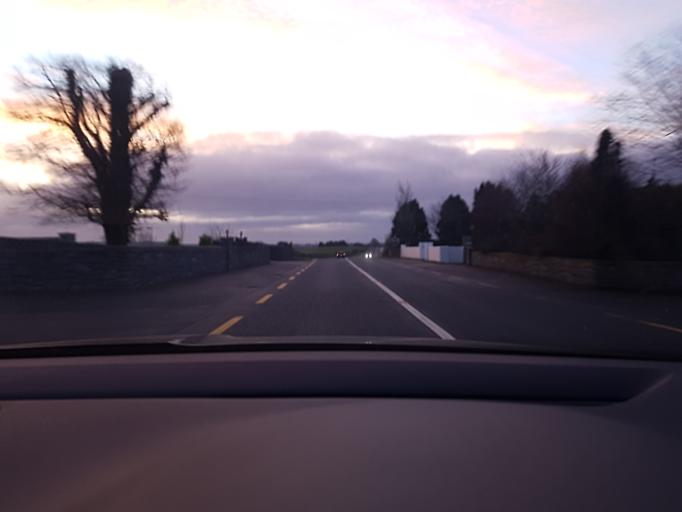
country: IE
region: Connaught
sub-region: County Galway
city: Tuam
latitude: 53.5452
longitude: -8.8935
